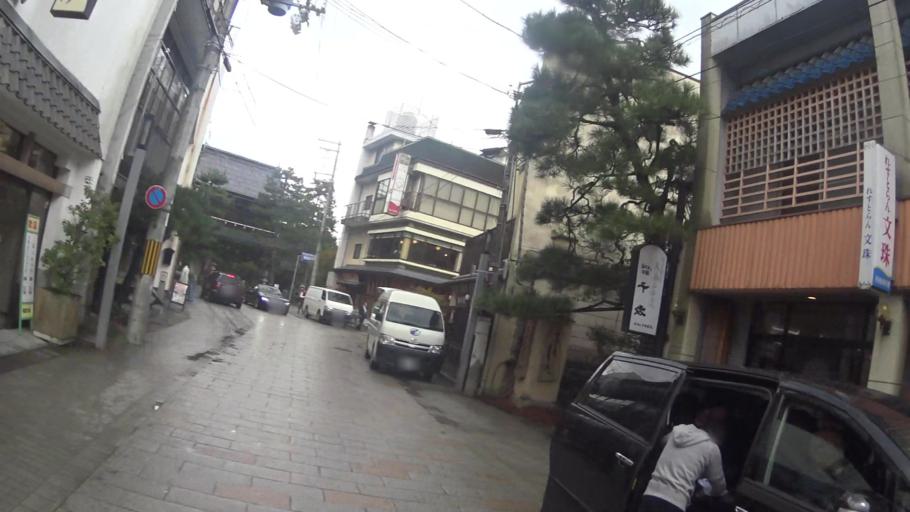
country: JP
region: Kyoto
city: Miyazu
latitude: 35.5571
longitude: 135.1835
